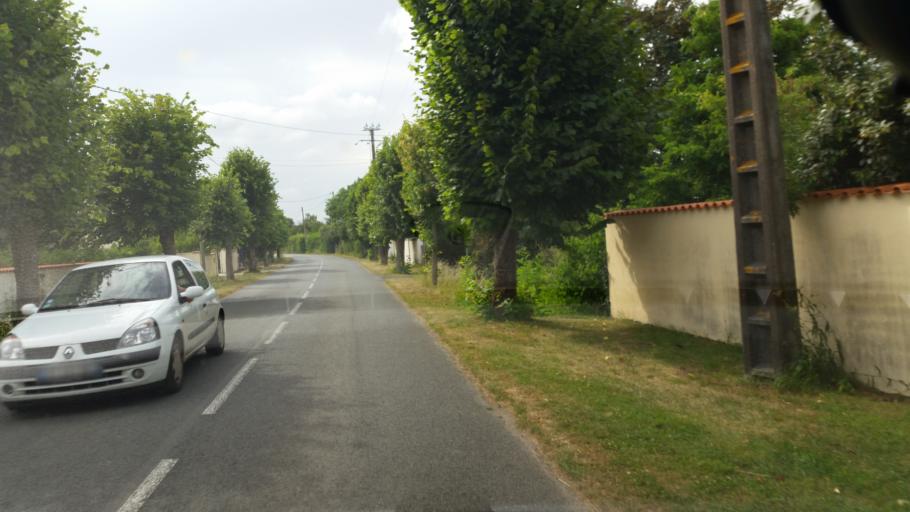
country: FR
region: Poitou-Charentes
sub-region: Departement de la Charente-Maritime
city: Saint-Jean-de-Liversay
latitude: 46.2129
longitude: -0.8774
